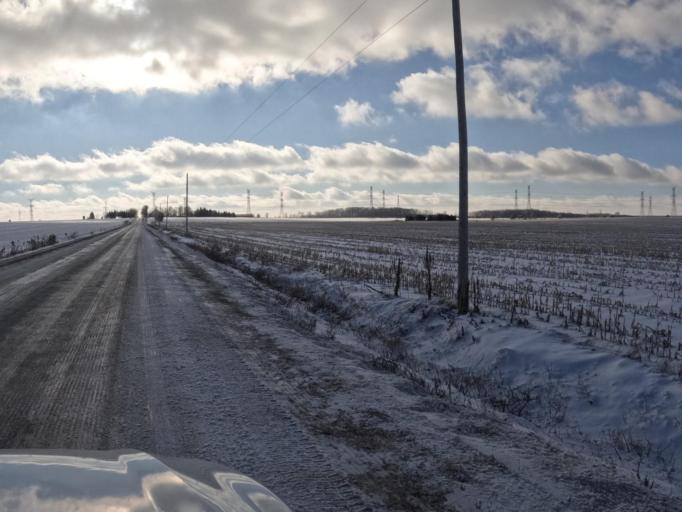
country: CA
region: Ontario
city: Shelburne
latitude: 44.0038
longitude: -80.4103
